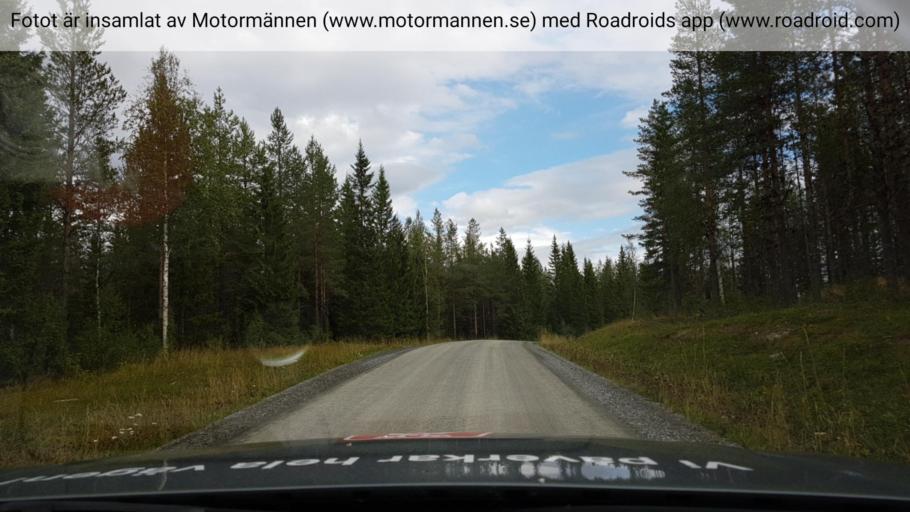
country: SE
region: Jaemtland
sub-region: Krokoms Kommun
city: Valla
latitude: 63.6646
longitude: 13.7221
